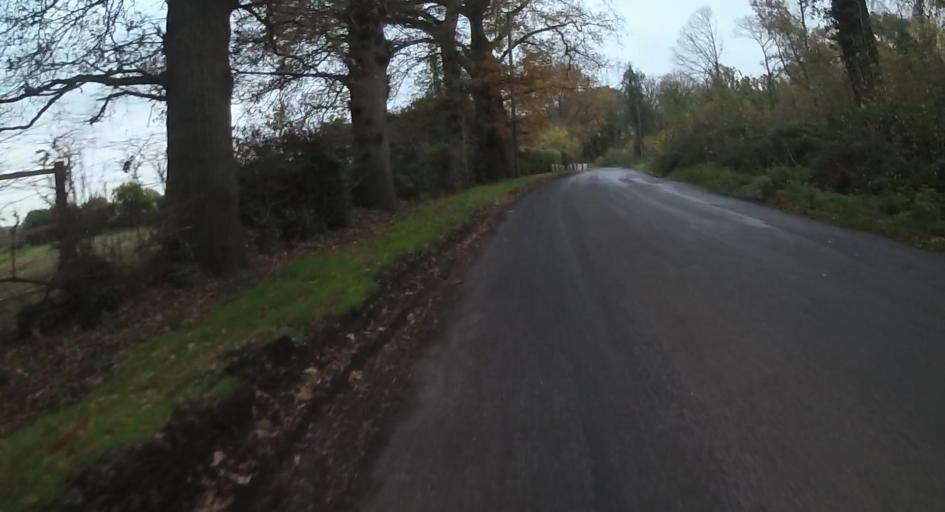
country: GB
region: England
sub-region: West Berkshire
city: Arborfield
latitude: 51.3850
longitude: -0.9328
